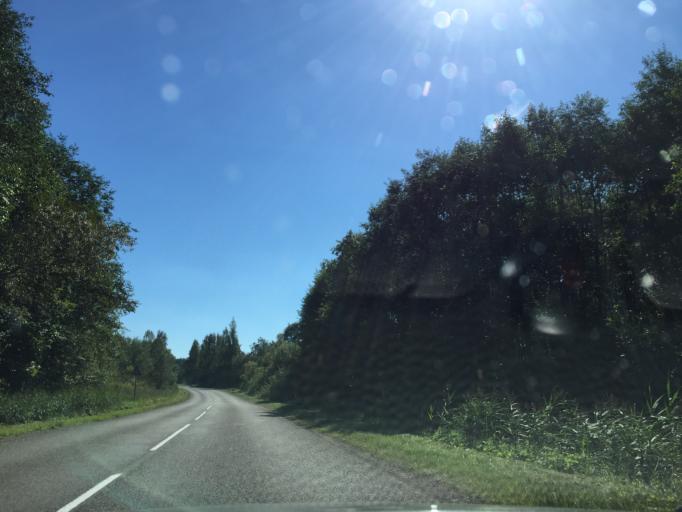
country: LV
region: Akniste
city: Akniste
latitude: 56.1235
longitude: 25.8309
